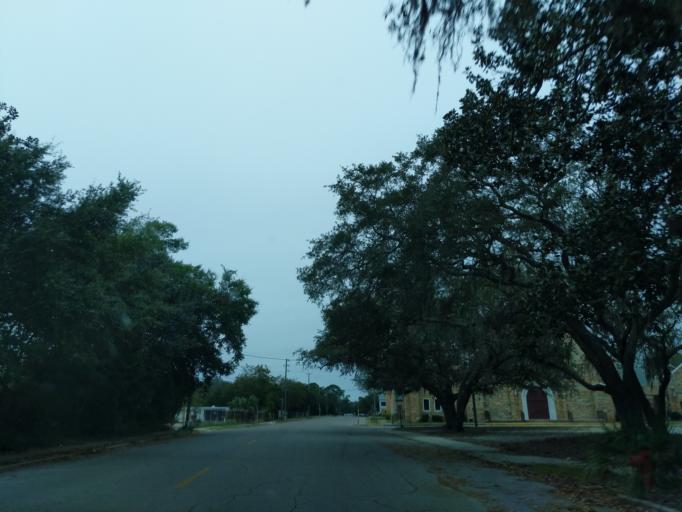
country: US
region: Florida
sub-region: Okaloosa County
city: Fort Walton Beach
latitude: 30.4053
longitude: -86.6081
